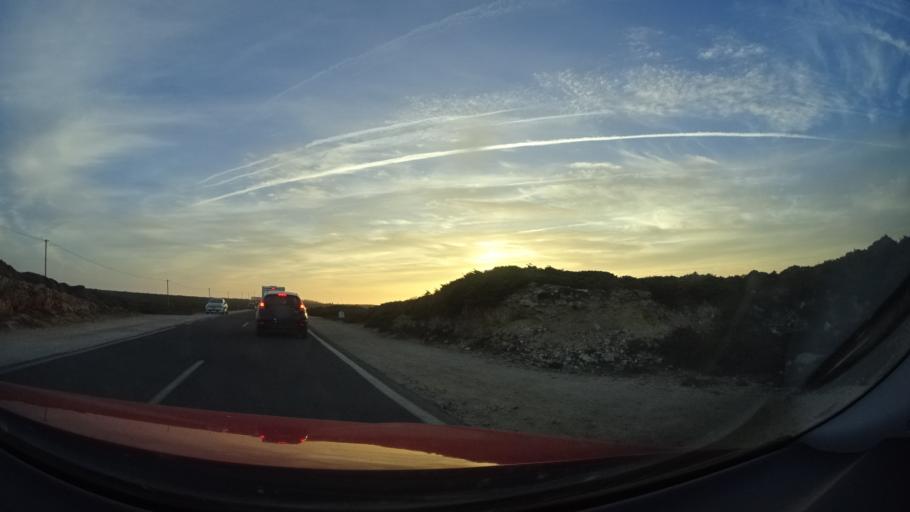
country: PT
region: Faro
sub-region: Vila do Bispo
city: Sagres
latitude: 37.0255
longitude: -8.9903
